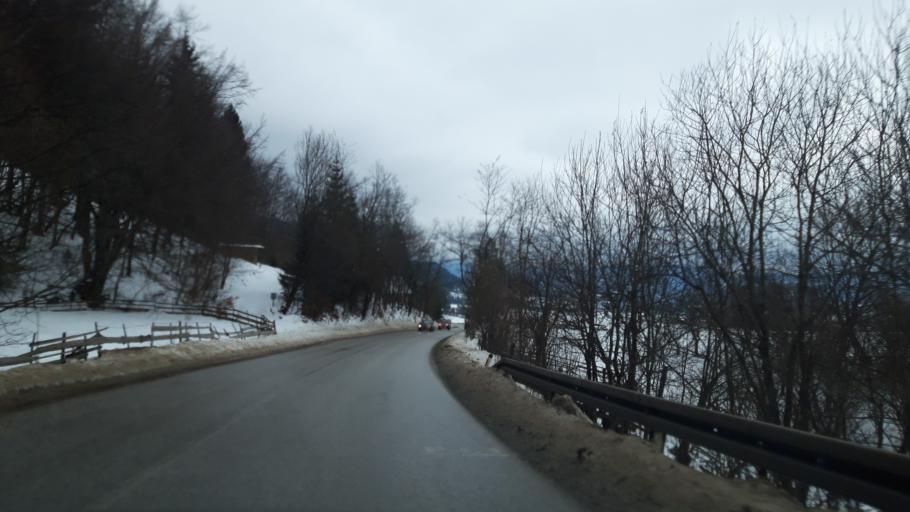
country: BA
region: Republika Srpska
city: Pale
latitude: 43.9009
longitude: 18.6364
